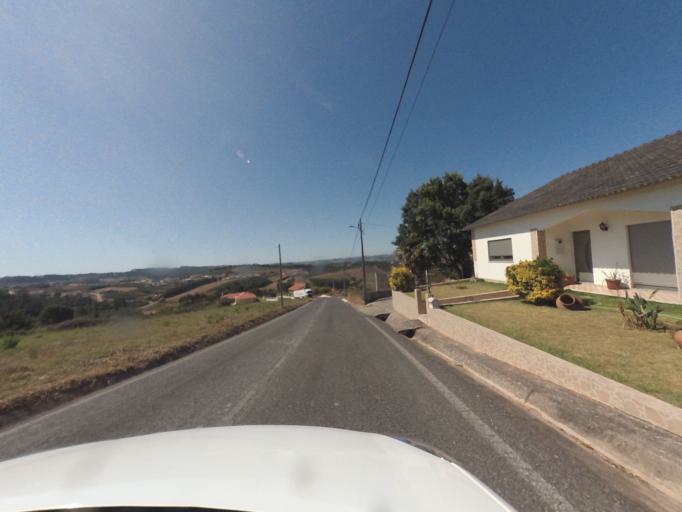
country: PT
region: Leiria
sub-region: Alcobaca
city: Turquel
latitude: 39.4853
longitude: -8.9900
